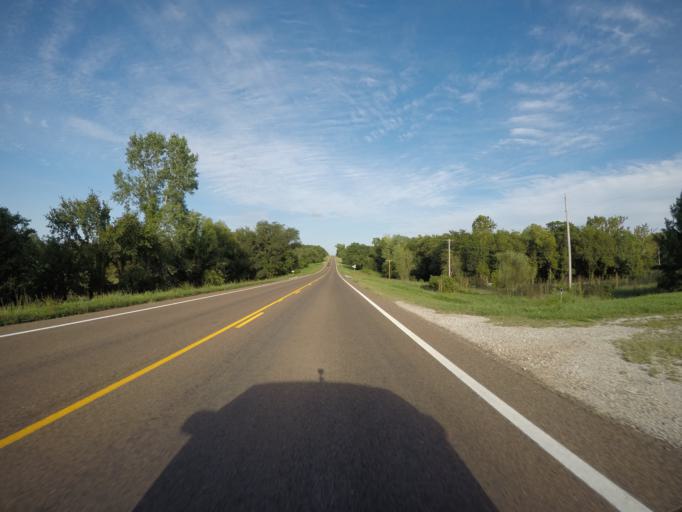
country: US
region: Kansas
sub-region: Douglas County
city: Lawrence
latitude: 39.0004
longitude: -95.1712
